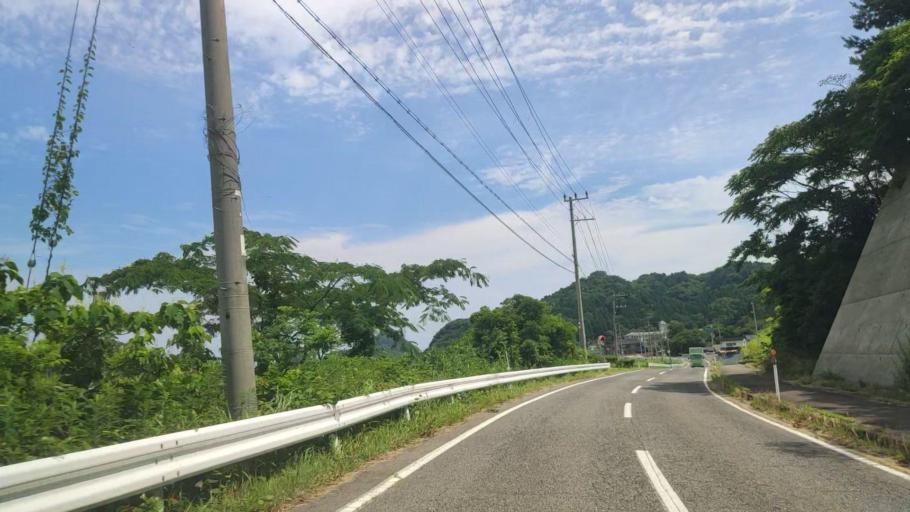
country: JP
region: Hyogo
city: Toyooka
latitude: 35.6454
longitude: 134.7624
